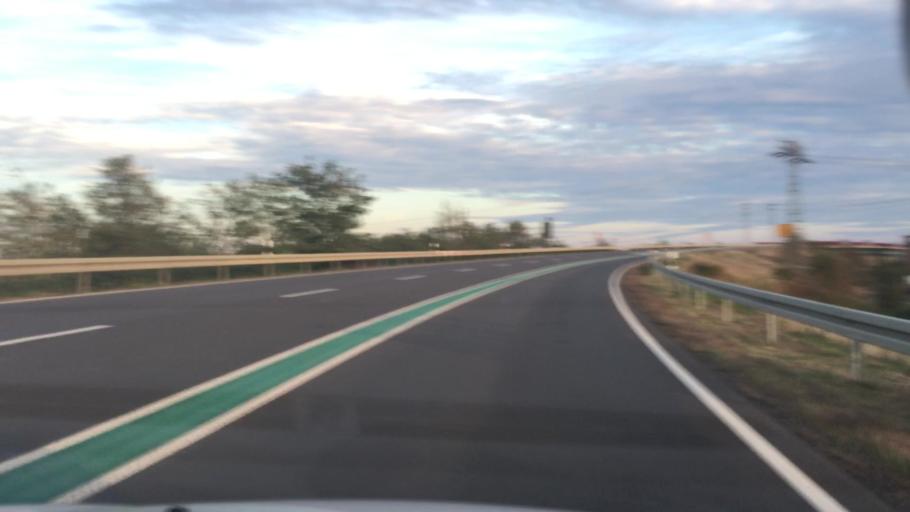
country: DE
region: Brandenburg
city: Senftenberg
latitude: 51.5344
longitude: 14.0112
